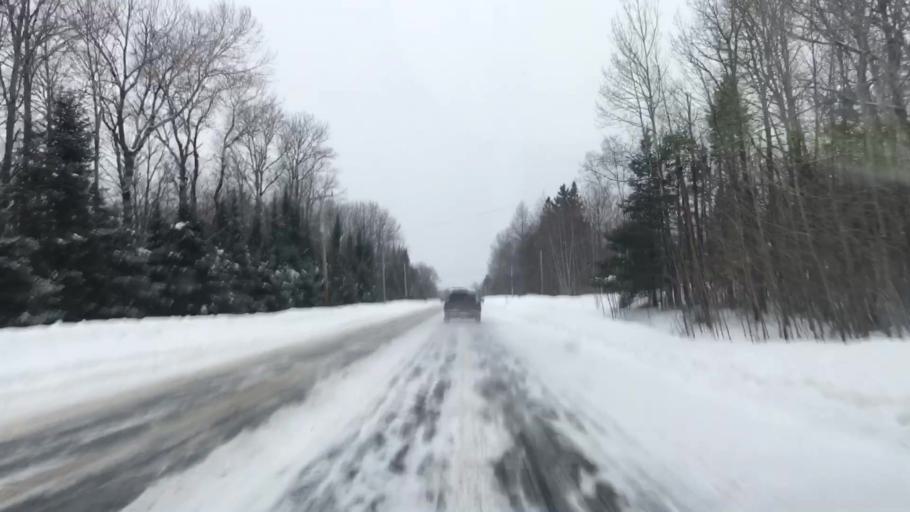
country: US
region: Maine
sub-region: Penobscot County
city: Medway
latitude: 45.5865
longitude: -68.4341
